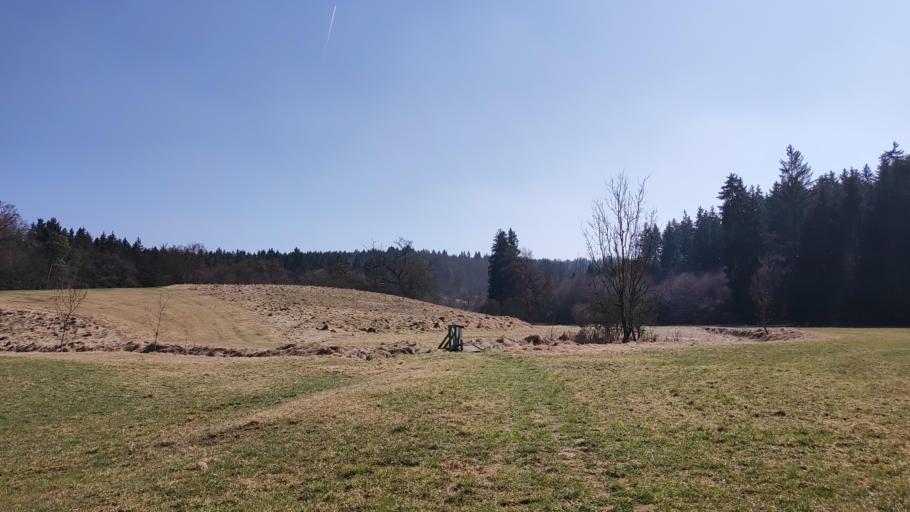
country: DE
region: Baden-Wuerttemberg
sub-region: Tuebingen Region
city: Borslingen
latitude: 48.5264
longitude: 10.0502
